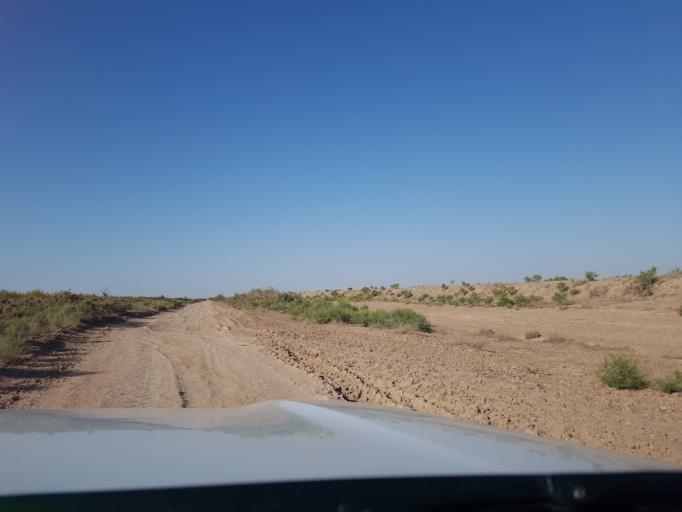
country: IR
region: Razavi Khorasan
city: Sarakhs
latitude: 36.9760
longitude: 61.3849
